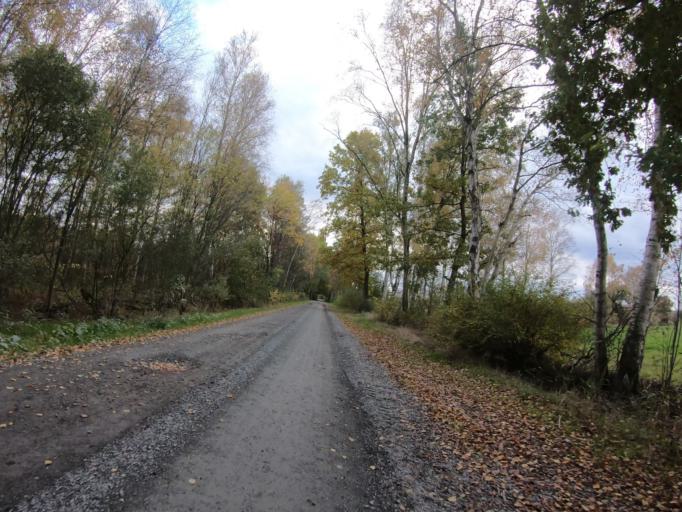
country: DE
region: Lower Saxony
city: Wagenhoff
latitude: 52.5565
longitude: 10.5582
